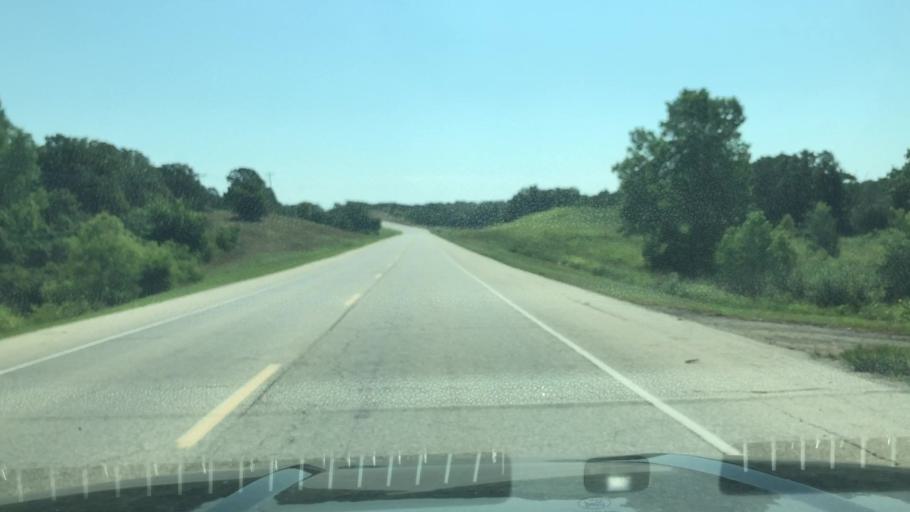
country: US
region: Oklahoma
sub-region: Creek County
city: Mannford
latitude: 36.0030
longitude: -96.4007
